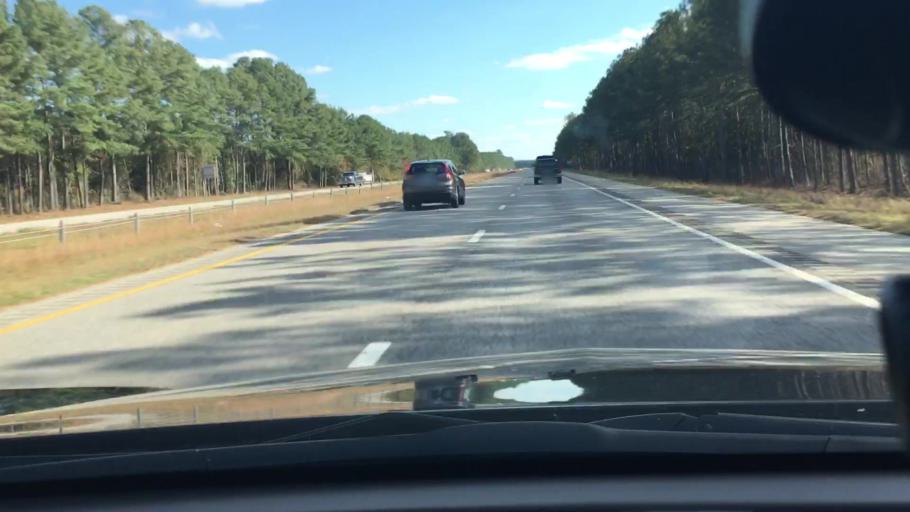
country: US
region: North Carolina
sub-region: Pitt County
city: Farmville
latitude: 35.6401
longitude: -77.7281
